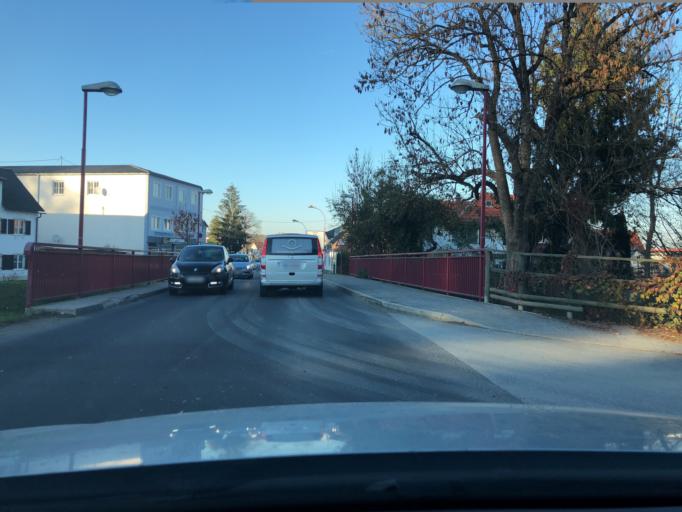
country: AT
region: Styria
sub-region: Politischer Bezirk Hartberg-Fuerstenfeld
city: Fuerstenfeld
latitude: 47.0551
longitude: 16.0726
